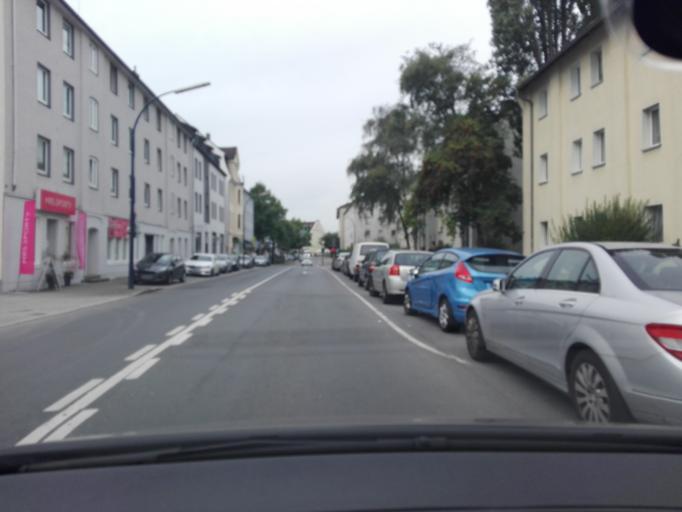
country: DE
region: North Rhine-Westphalia
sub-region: Regierungsbezirk Arnsberg
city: Holzwickede
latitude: 51.5035
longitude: 7.6192
